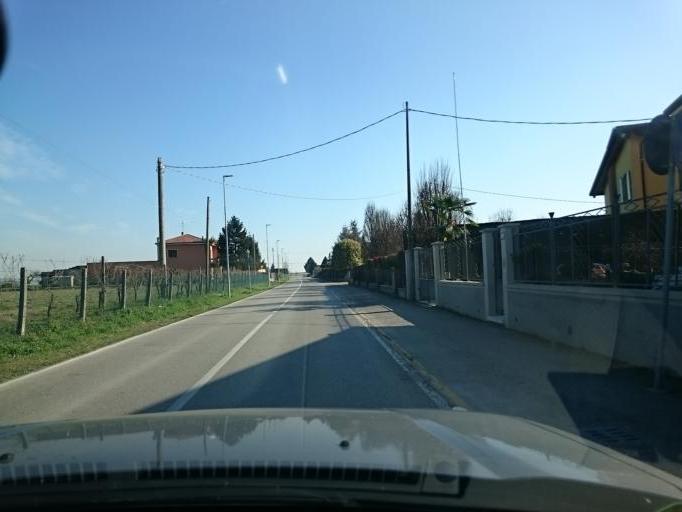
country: IT
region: Veneto
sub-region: Provincia di Verona
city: Vigasio
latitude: 45.3113
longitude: 10.9463
